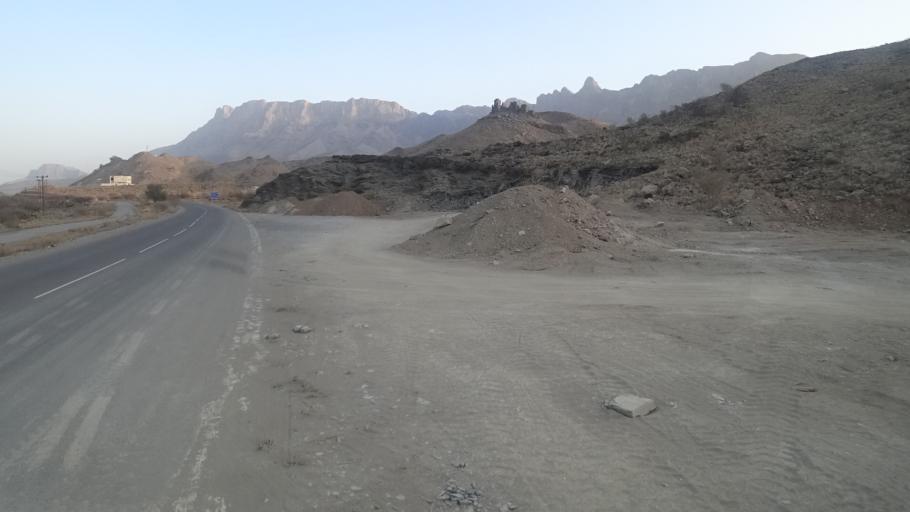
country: OM
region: Muhafazat ad Dakhiliyah
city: Bahla'
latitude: 23.1759
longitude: 57.1458
